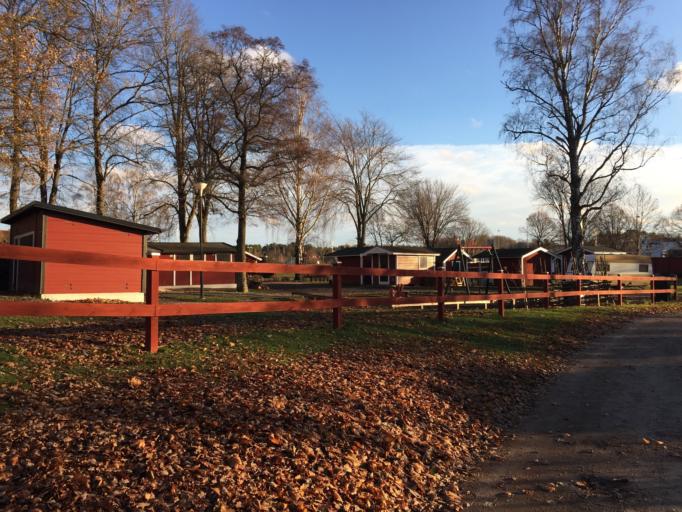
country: SE
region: OEstergoetland
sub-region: Soderkopings Kommun
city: Soederkoeping
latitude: 58.4774
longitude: 16.3334
